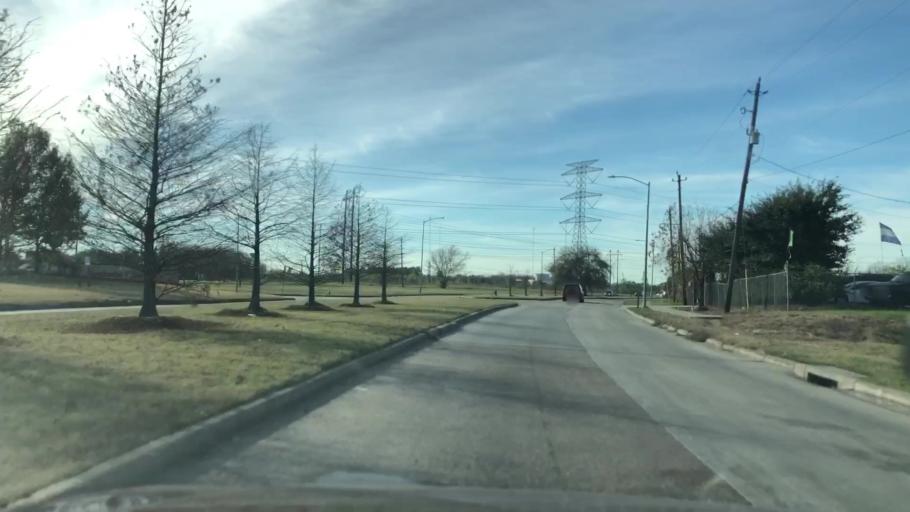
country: US
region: Texas
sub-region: Fort Bend County
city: Missouri City
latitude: 29.6314
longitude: -95.4934
